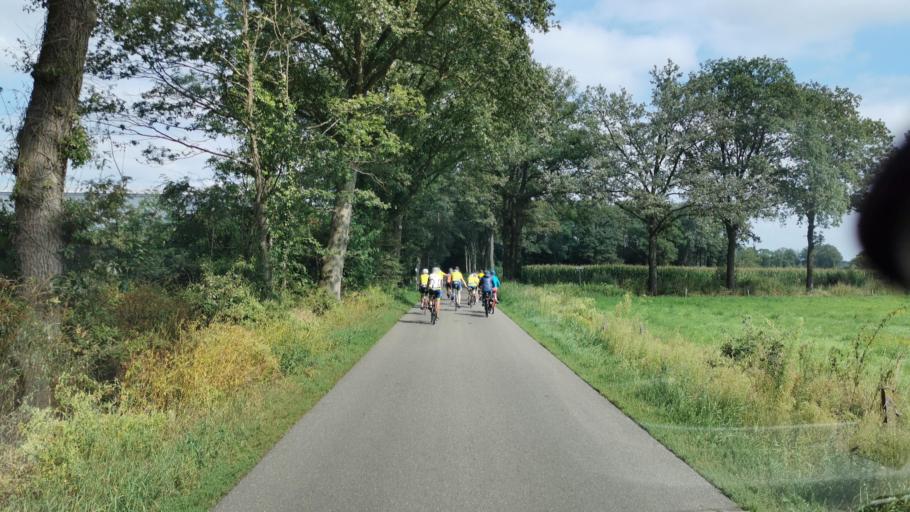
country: NL
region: Overijssel
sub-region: Gemeente Oldenzaal
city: Oldenzaal
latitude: 52.3410
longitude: 6.8933
